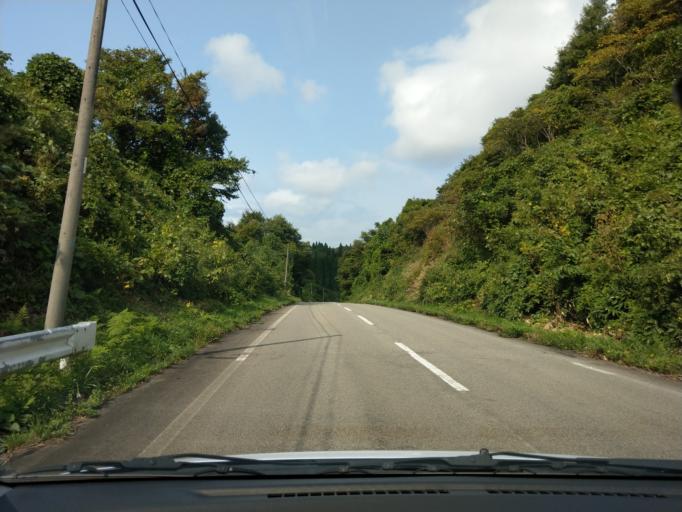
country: JP
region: Akita
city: Omagari
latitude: 39.4941
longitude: 140.3120
